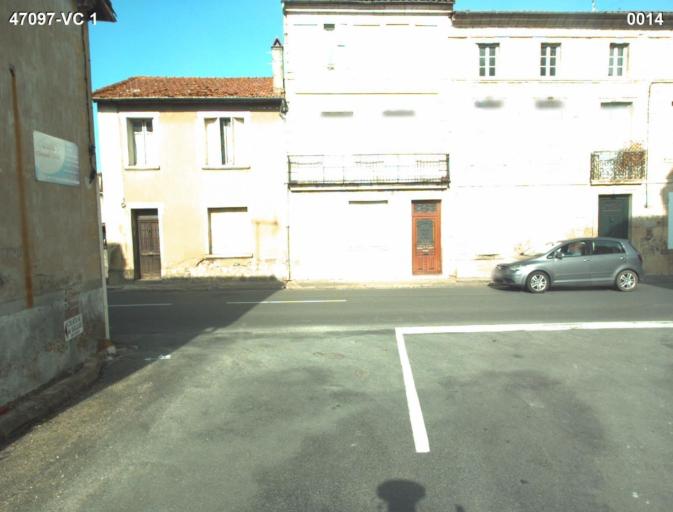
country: FR
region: Aquitaine
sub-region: Departement du Lot-et-Garonne
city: Vianne
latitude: 44.2210
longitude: 0.3463
